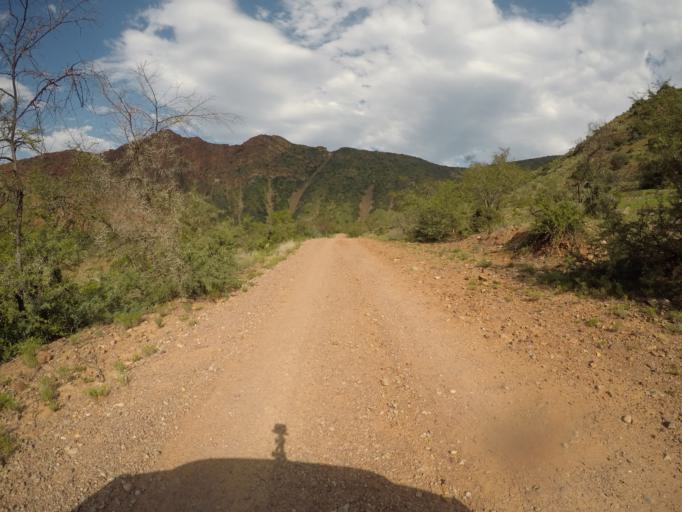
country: ZA
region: Eastern Cape
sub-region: Cacadu District Municipality
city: Kareedouw
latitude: -33.6394
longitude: 24.3168
